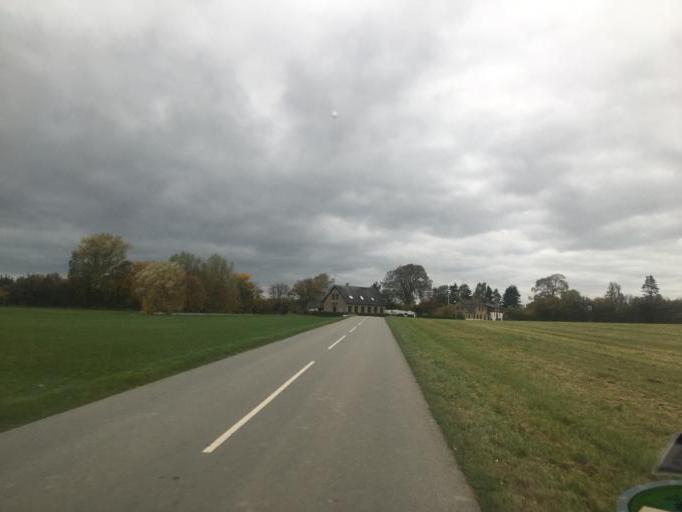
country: DK
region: Zealand
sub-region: Koge Kommune
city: Bjaeverskov
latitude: 55.4231
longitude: 11.9818
